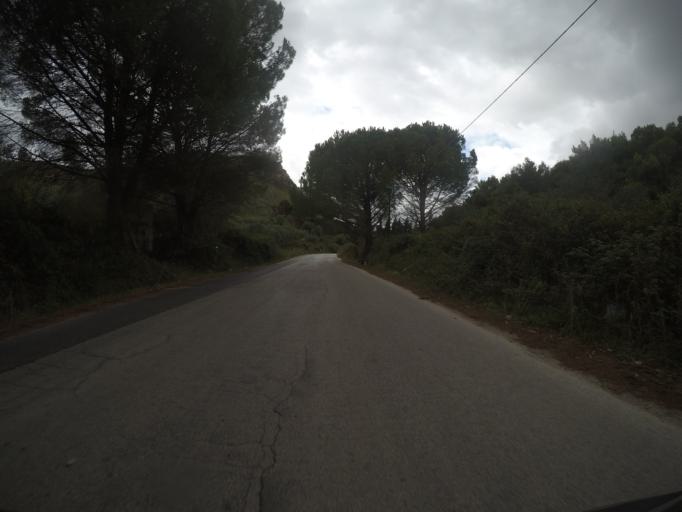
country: IT
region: Sicily
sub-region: Palermo
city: Montelepre
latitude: 38.1010
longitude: 13.1705
